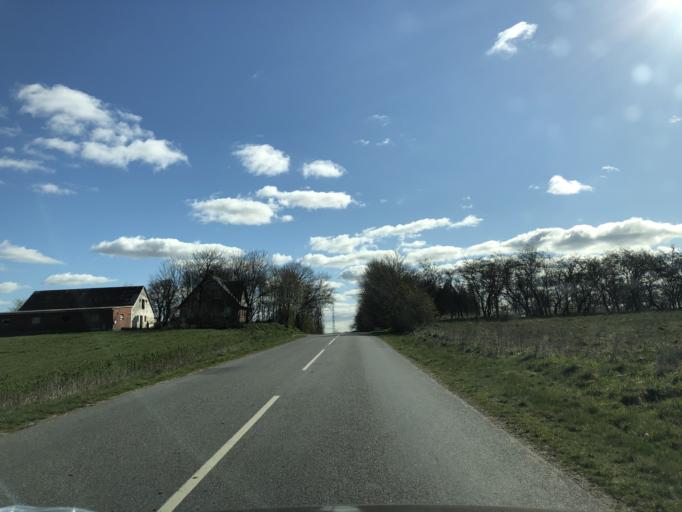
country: DK
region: North Denmark
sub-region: Vesthimmerland Kommune
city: Alestrup
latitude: 56.6063
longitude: 9.5660
